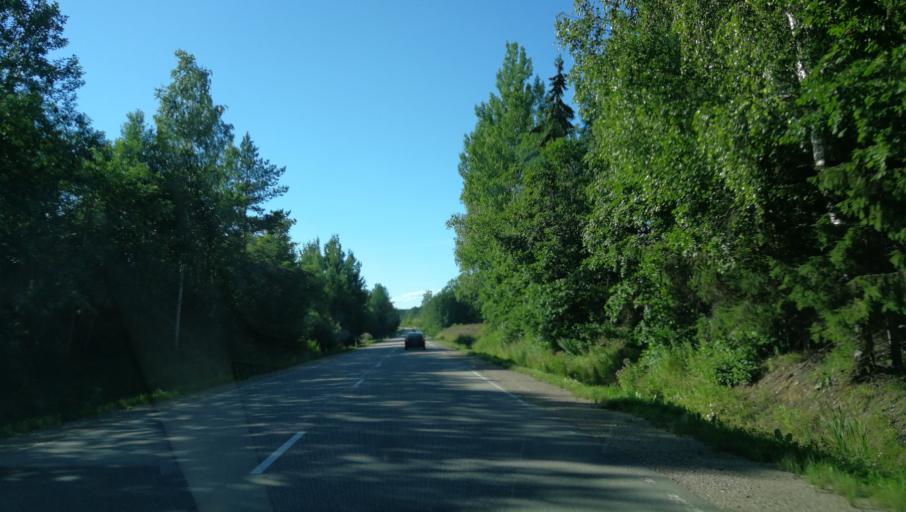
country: LV
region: Vecpiebalga
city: Vecpiebalga
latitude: 57.1008
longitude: 25.7233
